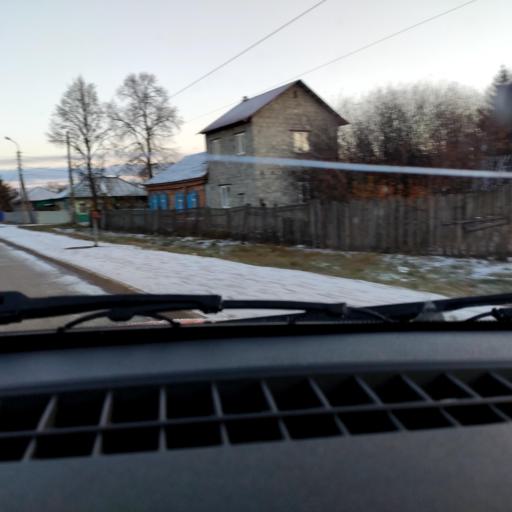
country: RU
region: Bashkortostan
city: Avdon
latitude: 54.7060
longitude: 55.8172
